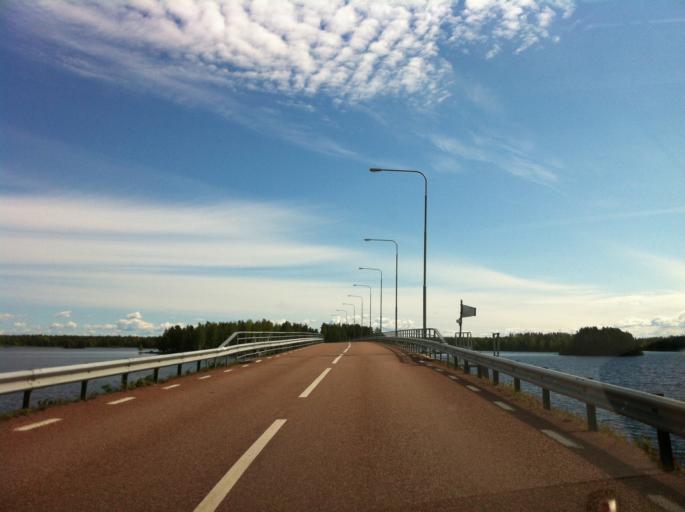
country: SE
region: Dalarna
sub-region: Mora Kommun
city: Mora
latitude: 60.8944
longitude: 14.5561
